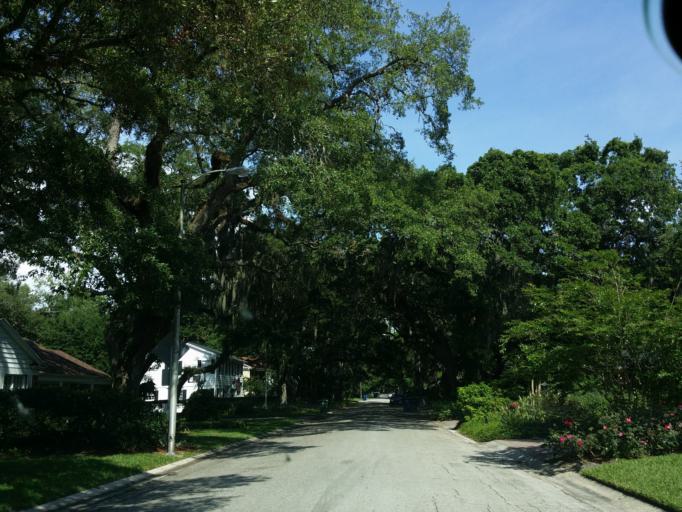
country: US
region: Florida
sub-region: Hillsborough County
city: Tampa
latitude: 27.9327
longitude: -82.5231
